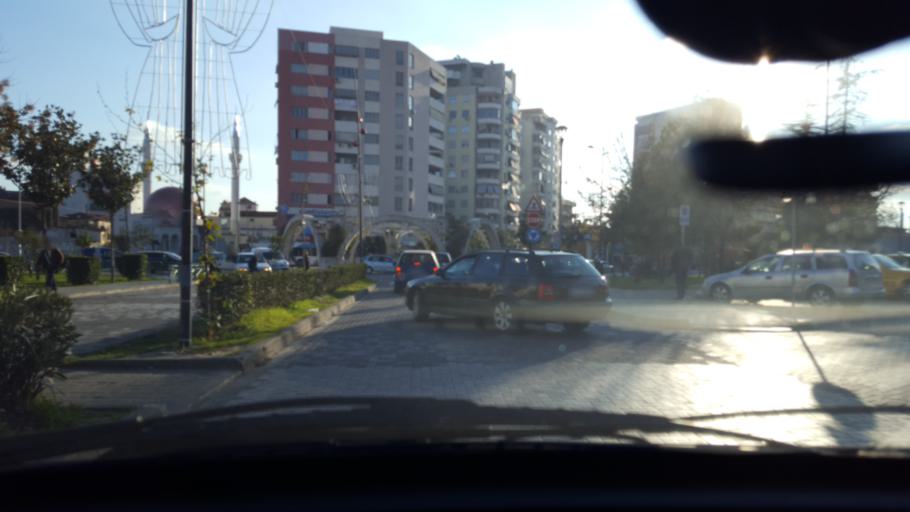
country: AL
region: Elbasan
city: Elbasan
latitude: 41.1112
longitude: 20.0796
